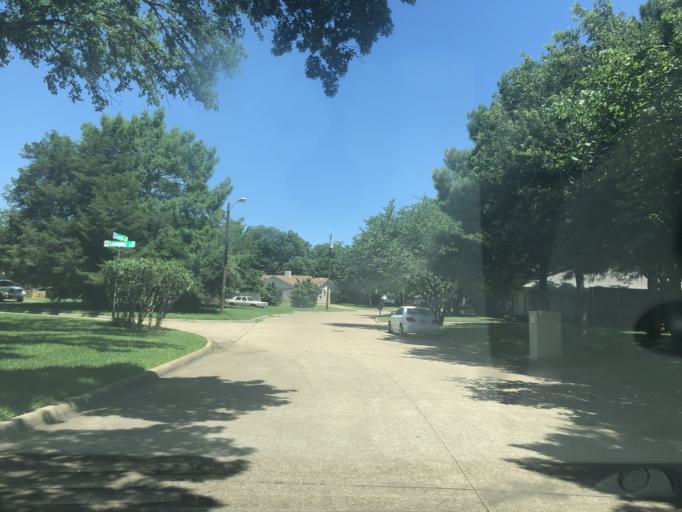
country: US
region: Texas
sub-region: Dallas County
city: Grand Prairie
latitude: 32.7749
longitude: -97.0409
